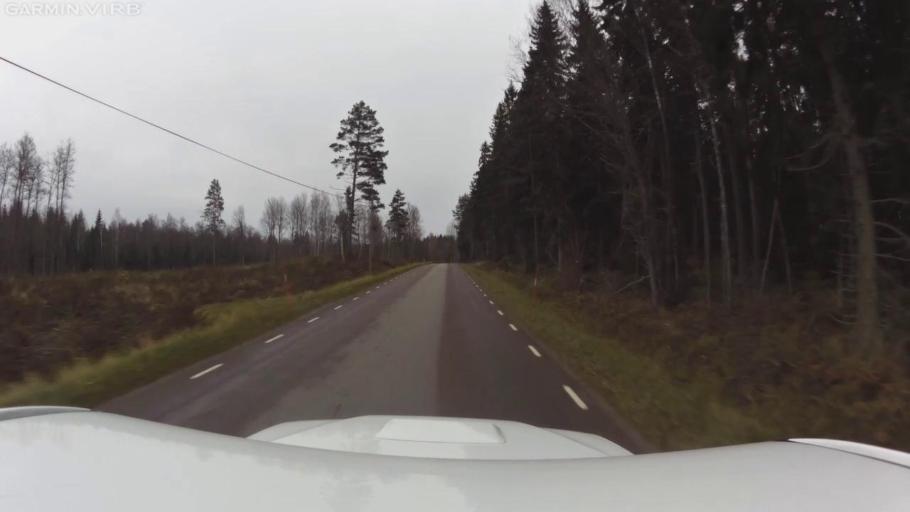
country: SE
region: OEstergoetland
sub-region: Linkopings Kommun
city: Vikingstad
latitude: 58.2483
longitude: 15.3866
